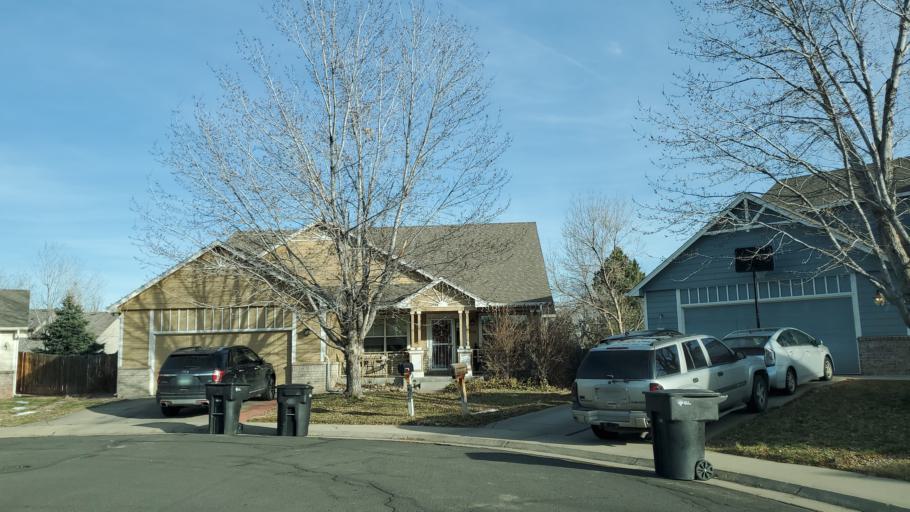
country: US
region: Colorado
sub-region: Adams County
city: Northglenn
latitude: 39.9060
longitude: -104.9576
